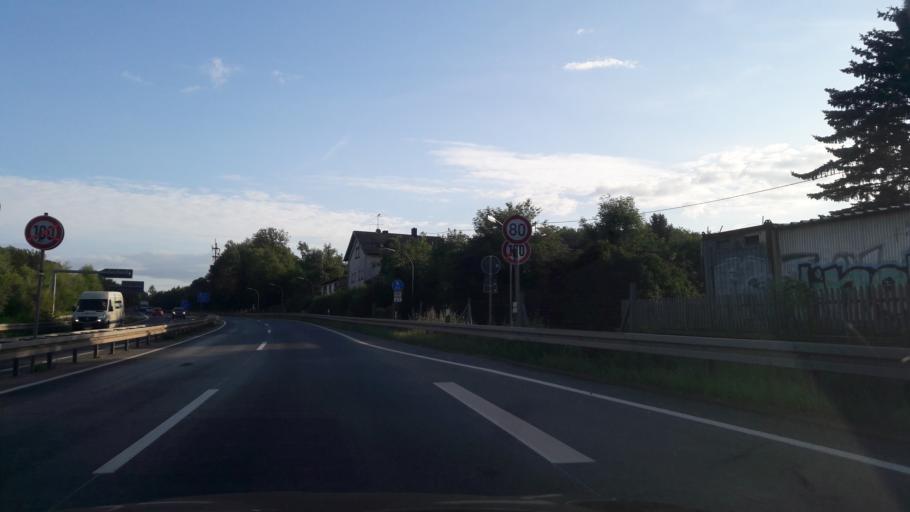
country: DE
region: Saarland
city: Riegelsberg
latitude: 49.2770
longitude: 6.9628
